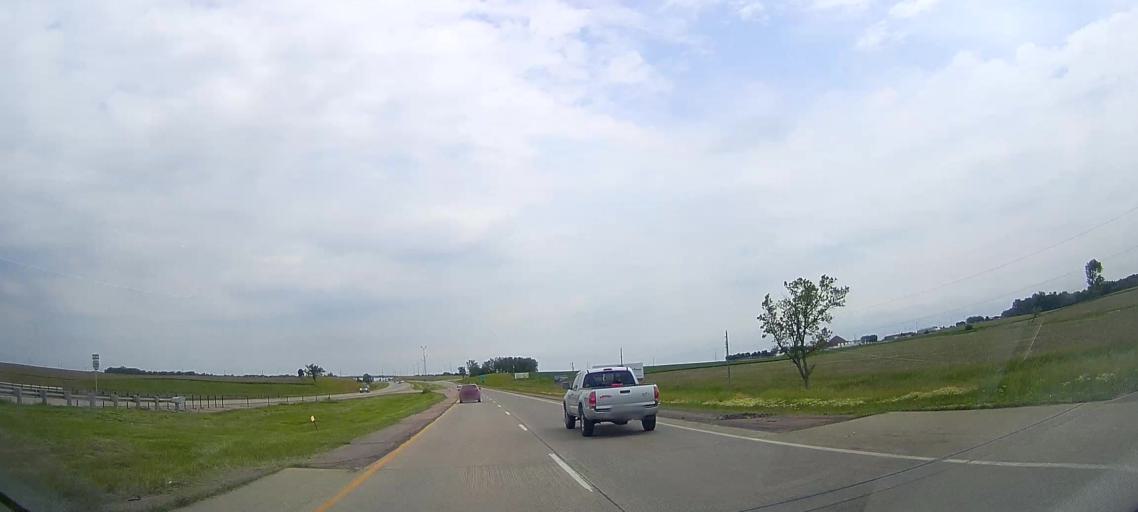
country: US
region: South Dakota
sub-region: Minnehaha County
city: Crooks
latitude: 43.6086
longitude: -96.8049
